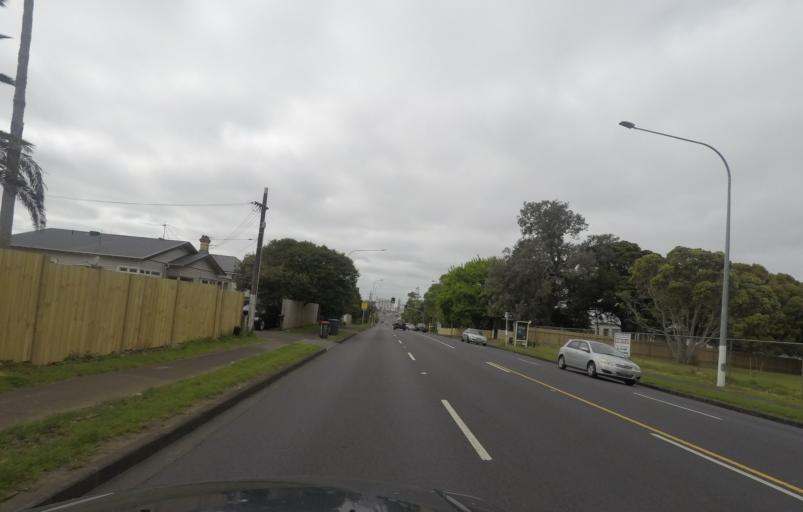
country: NZ
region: Auckland
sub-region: Auckland
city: Wiri
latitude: -36.9533
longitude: 174.8469
